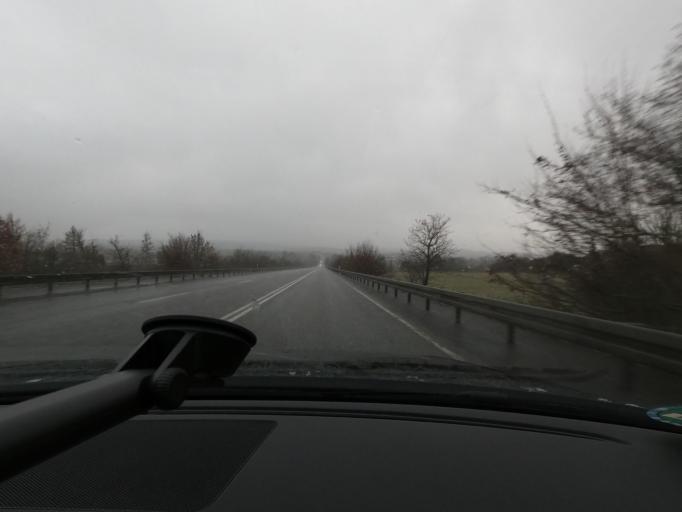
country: DE
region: Thuringia
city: Dingelstadt
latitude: 51.3180
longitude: 10.3286
